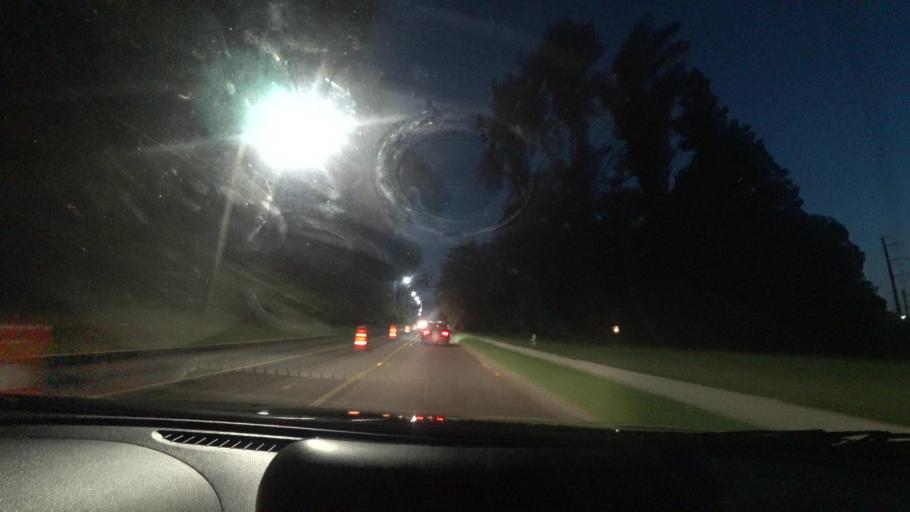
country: US
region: Georgia
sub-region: Fulton County
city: Atlanta
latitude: 33.8072
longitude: -84.4083
